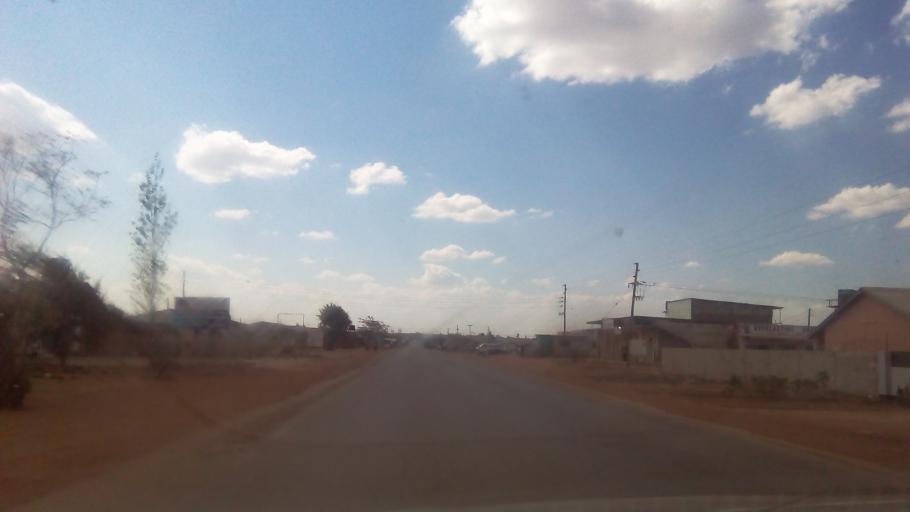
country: ZM
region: Lusaka
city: Lusaka
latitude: -15.4685
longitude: 28.3421
